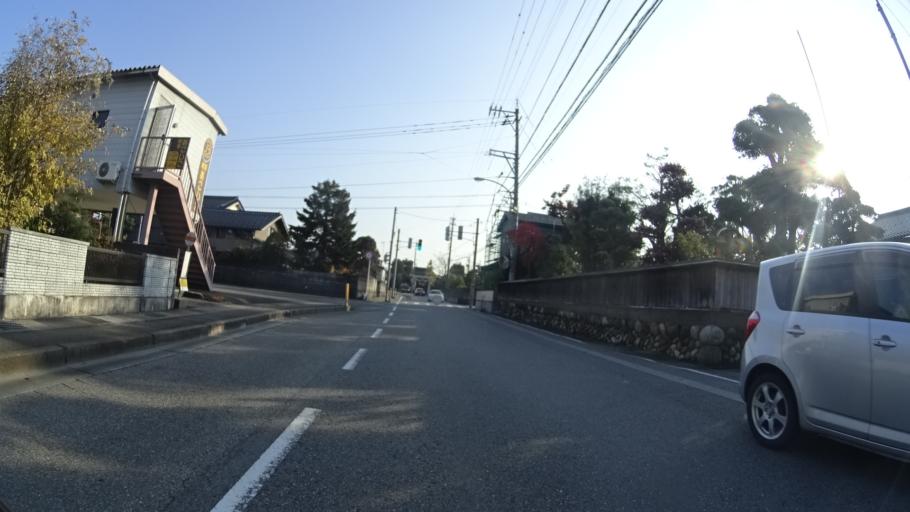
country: JP
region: Toyama
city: Toyama-shi
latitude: 36.6870
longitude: 137.2710
